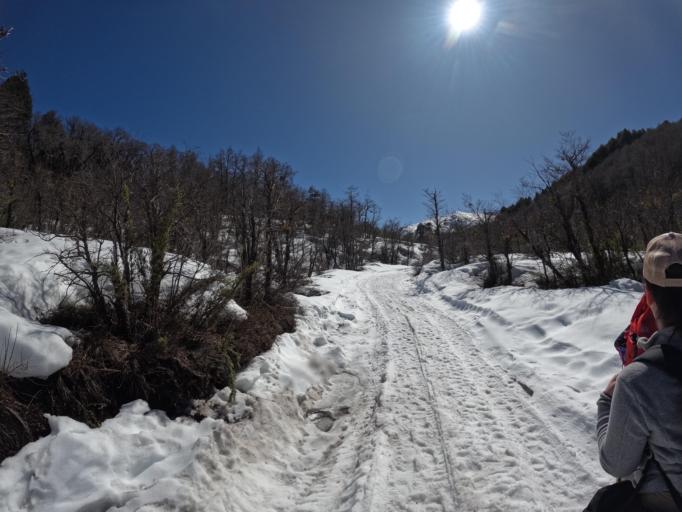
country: CL
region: Araucania
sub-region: Provincia de Cautin
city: Vilcun
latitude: -38.6647
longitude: -71.6196
